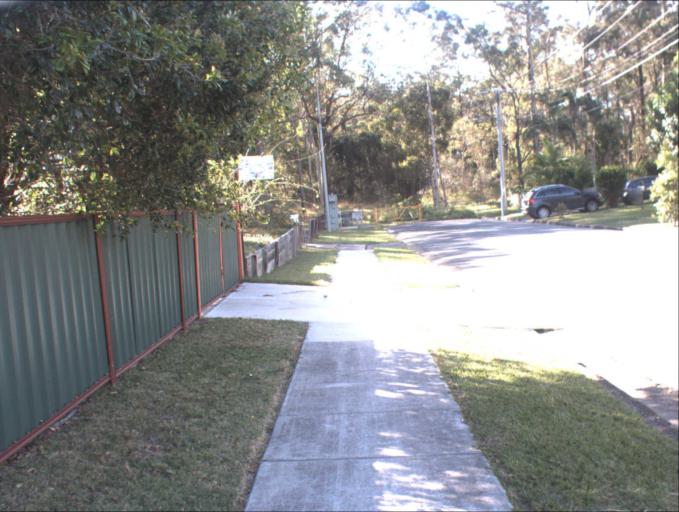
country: AU
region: Queensland
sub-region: Logan
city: Woodridge
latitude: -27.6247
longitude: 153.0976
